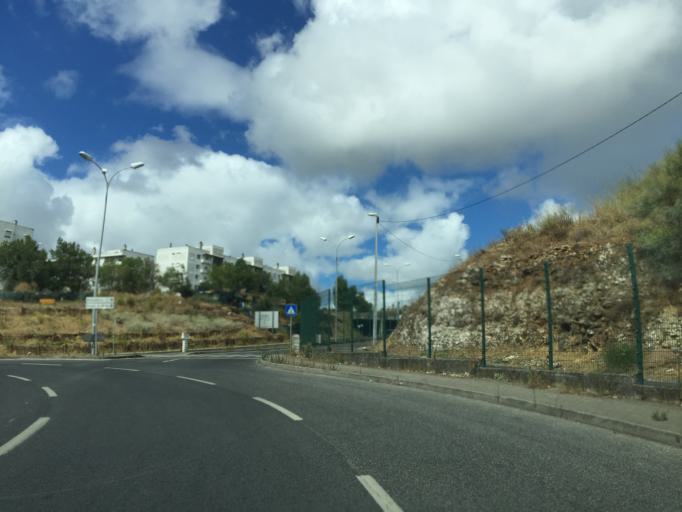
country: PT
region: Lisbon
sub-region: Amadora
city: Amadora
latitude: 38.7720
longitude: -9.2252
